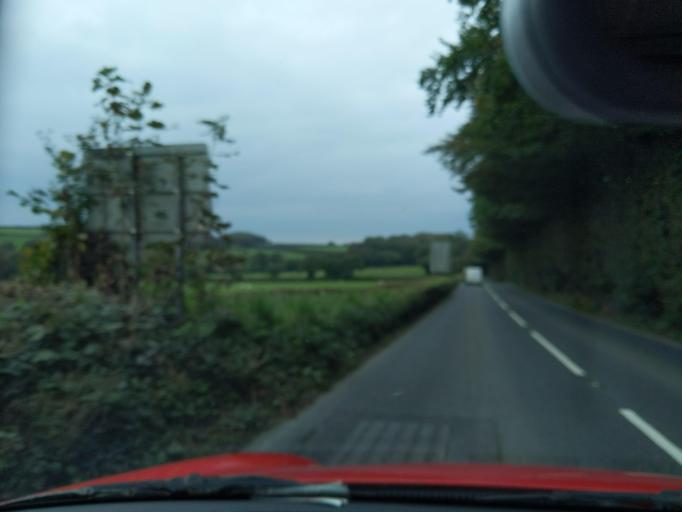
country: GB
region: England
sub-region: Devon
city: Okehampton
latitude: 50.7312
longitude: -4.0416
